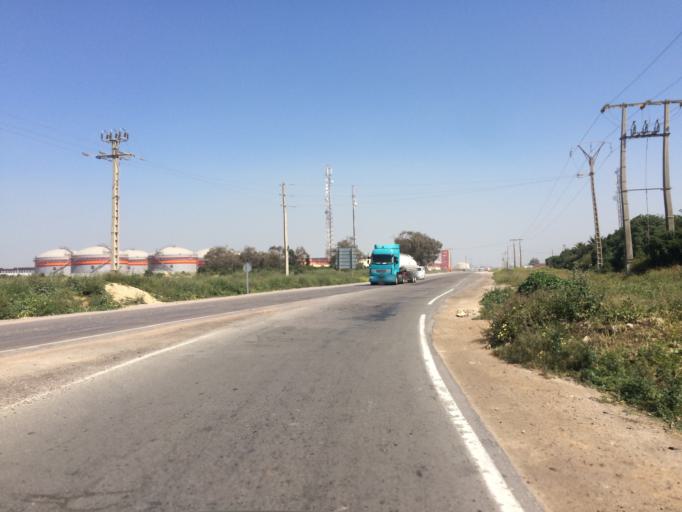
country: MA
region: Doukkala-Abda
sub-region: El-Jadida
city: Moulay Abdallah
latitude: 33.1378
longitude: -8.6094
